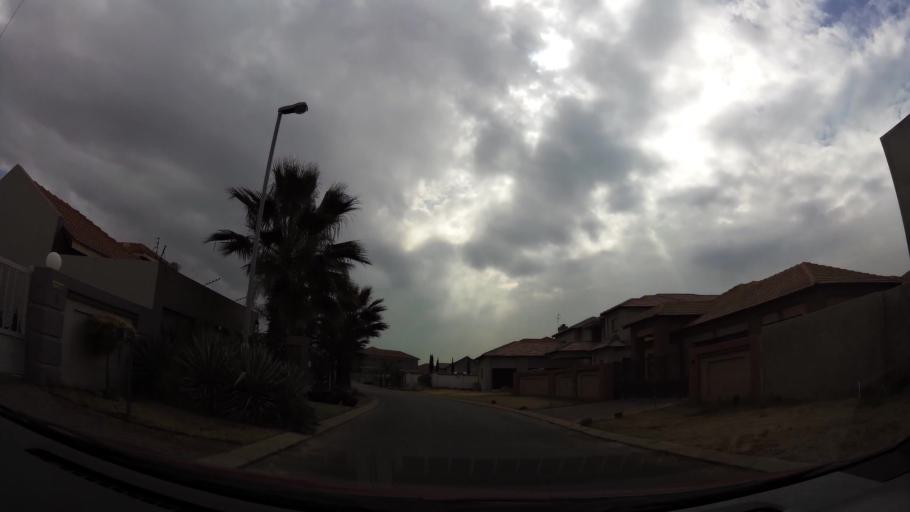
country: ZA
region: Gauteng
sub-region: Sedibeng District Municipality
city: Vanderbijlpark
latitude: -26.7274
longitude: 27.8676
